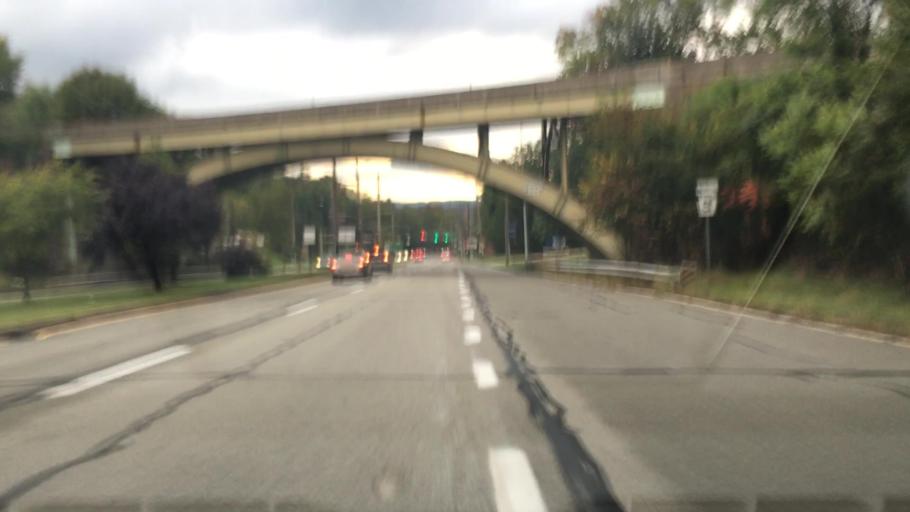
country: US
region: Pennsylvania
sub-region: Allegheny County
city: Edgewood
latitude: 40.4346
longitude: -79.8690
